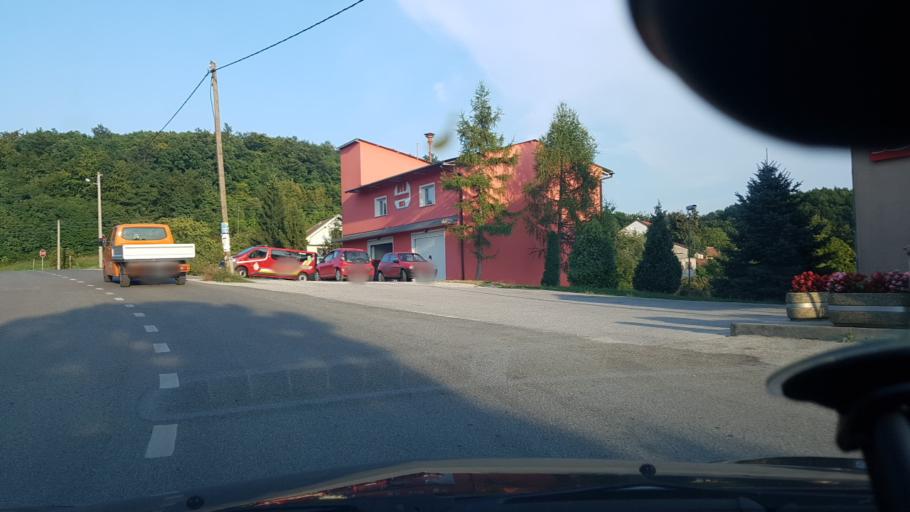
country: HR
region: Krapinsko-Zagorska
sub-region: Grad Krapina
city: Krapina
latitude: 46.1679
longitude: 15.8432
